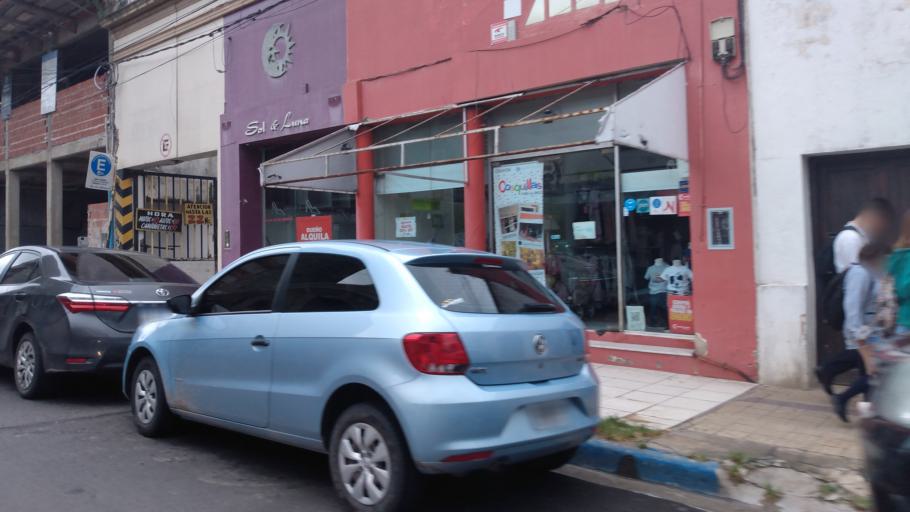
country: AR
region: Corrientes
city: Corrientes
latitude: -27.4687
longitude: -58.8332
